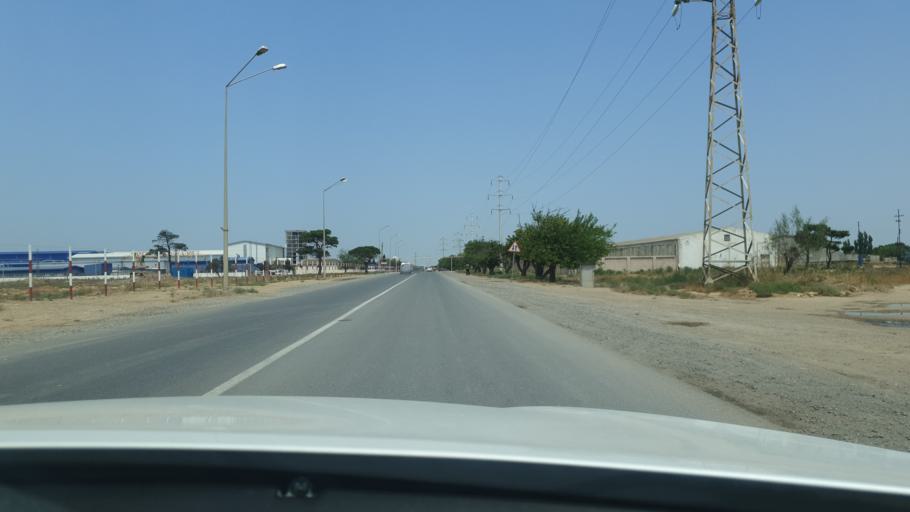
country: AZ
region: Baki
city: Qaracuxur
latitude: 40.3964
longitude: 49.9989
